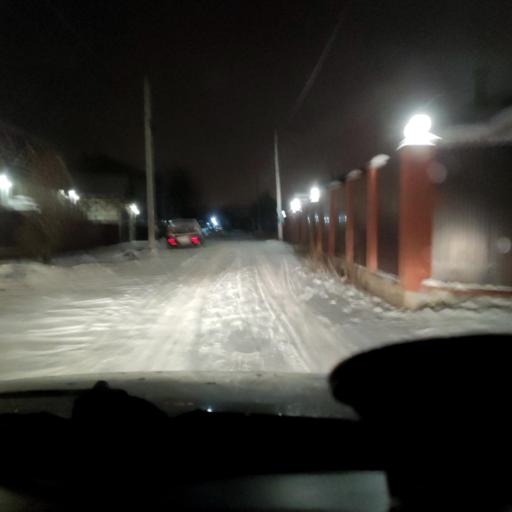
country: RU
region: Perm
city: Perm
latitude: 57.9906
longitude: 56.3082
